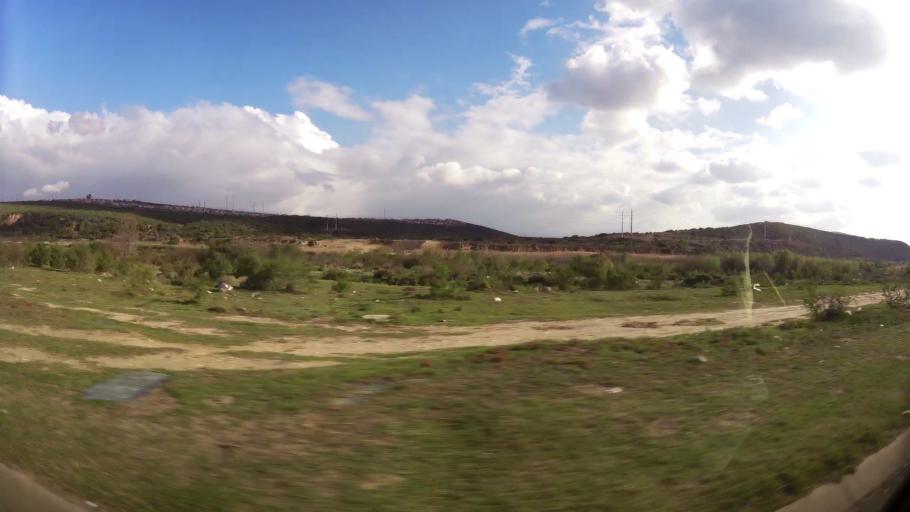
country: ZA
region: Eastern Cape
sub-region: Nelson Mandela Bay Metropolitan Municipality
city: Uitenhage
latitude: -33.7860
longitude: 25.4019
